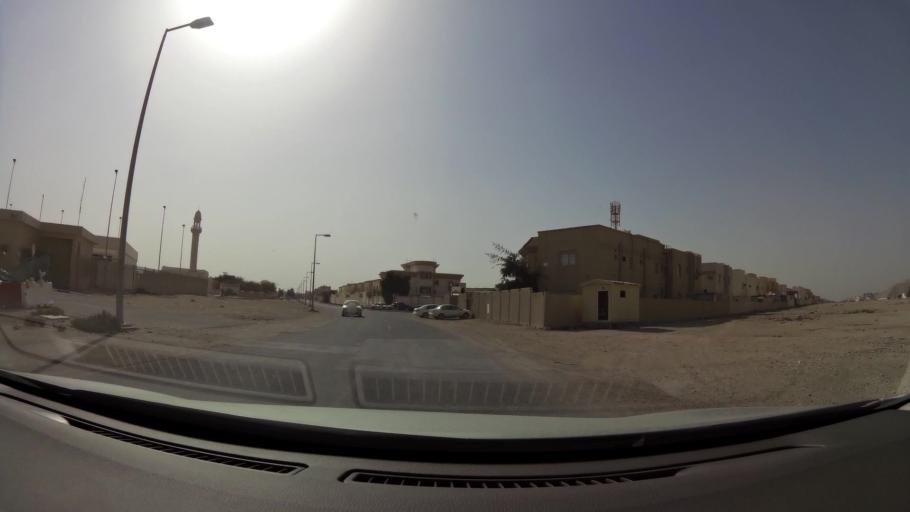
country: QA
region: Baladiyat ar Rayyan
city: Ar Rayyan
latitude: 25.3522
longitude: 51.4473
